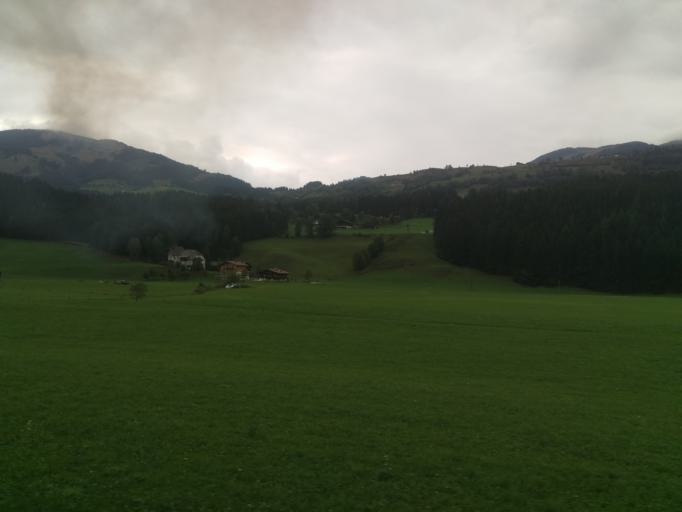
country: AT
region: Salzburg
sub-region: Politischer Bezirk Zell am See
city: Hollersbach im Pinzgau
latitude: 47.2796
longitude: 12.4352
